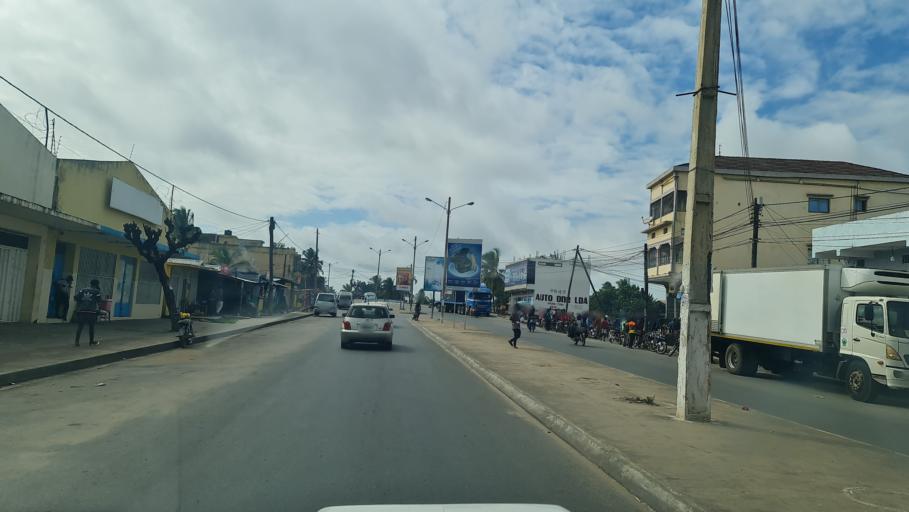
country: MZ
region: Nampula
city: Nampula
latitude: -15.1148
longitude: 39.2799
